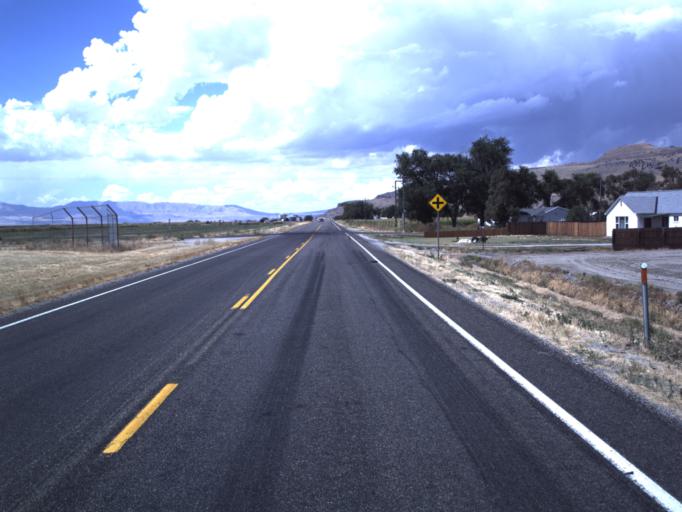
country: US
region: Utah
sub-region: Box Elder County
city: Elwood
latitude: 41.5689
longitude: -112.1961
